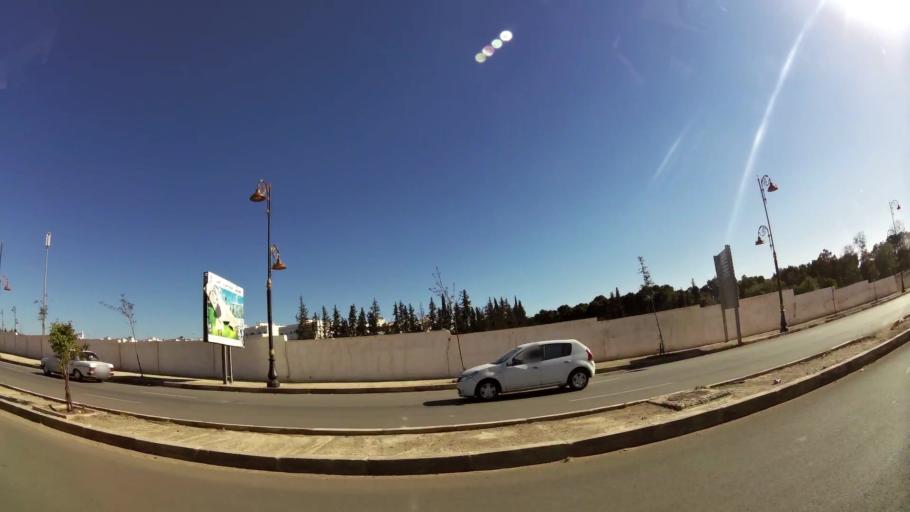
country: MA
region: Fes-Boulemane
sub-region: Fes
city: Fes
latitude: 33.9913
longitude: -5.0166
